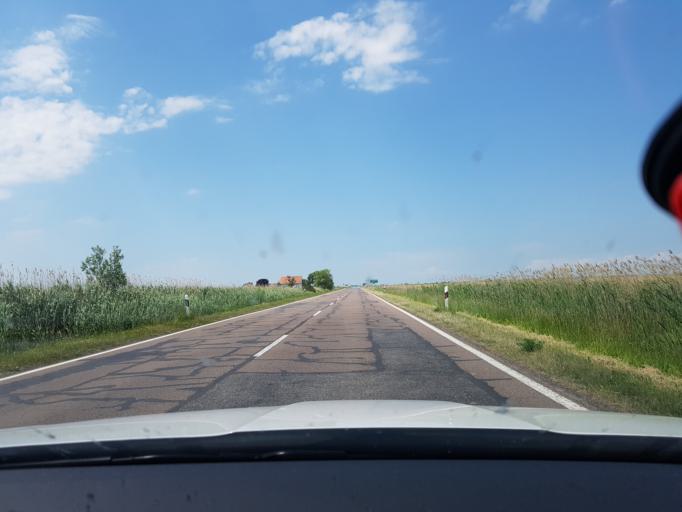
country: HU
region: Hajdu-Bihar
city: Hortobagy
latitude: 47.5901
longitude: 21.0857
